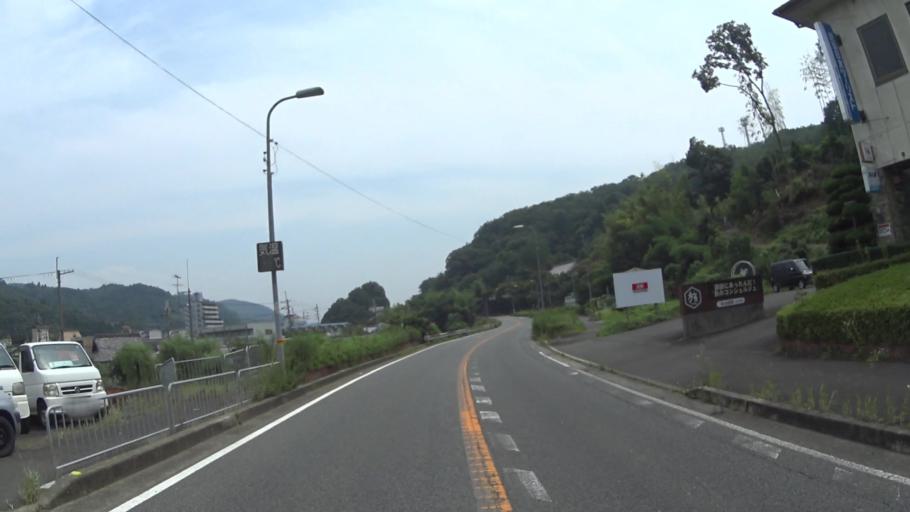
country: JP
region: Kyoto
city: Kameoka
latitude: 35.1090
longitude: 135.4778
